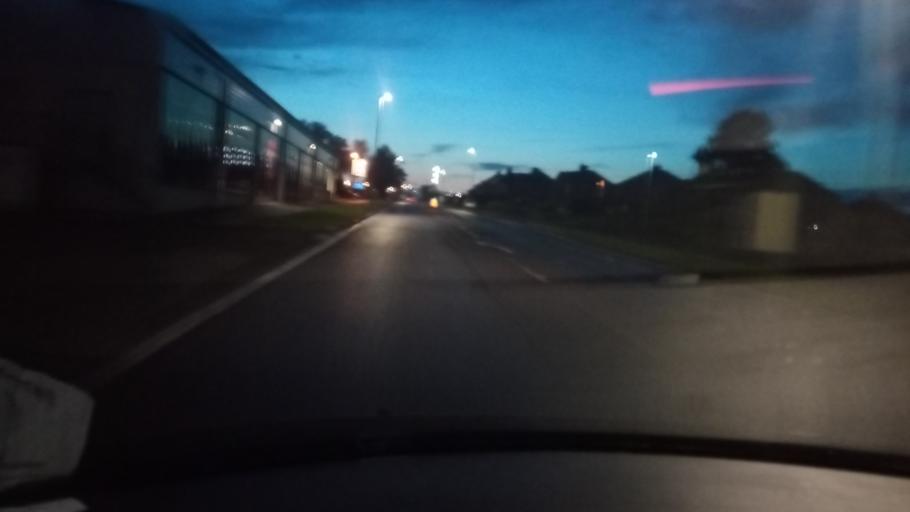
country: GB
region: England
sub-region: Northumberland
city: Berwick-Upon-Tweed
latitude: 55.7818
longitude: -2.0118
